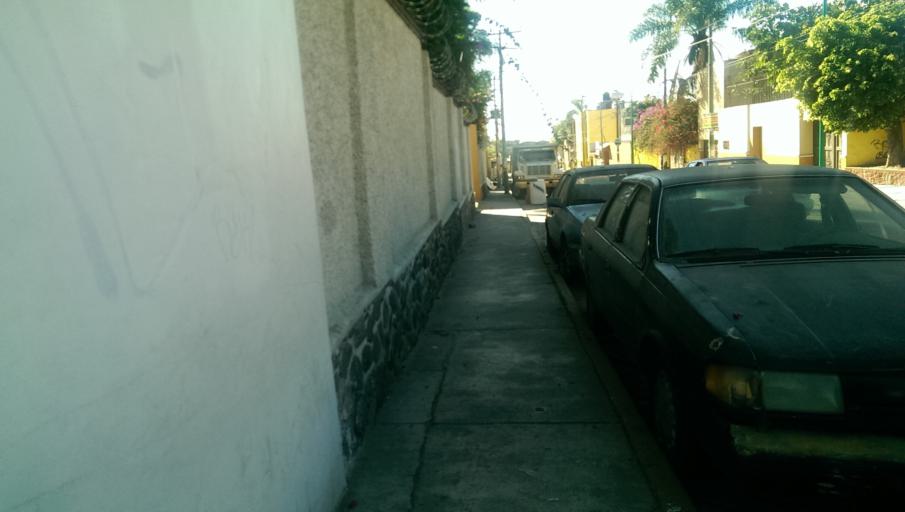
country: MX
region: Morelos
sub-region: Cuernavaca
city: Cuernavaca
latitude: 18.9241
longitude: -99.2420
